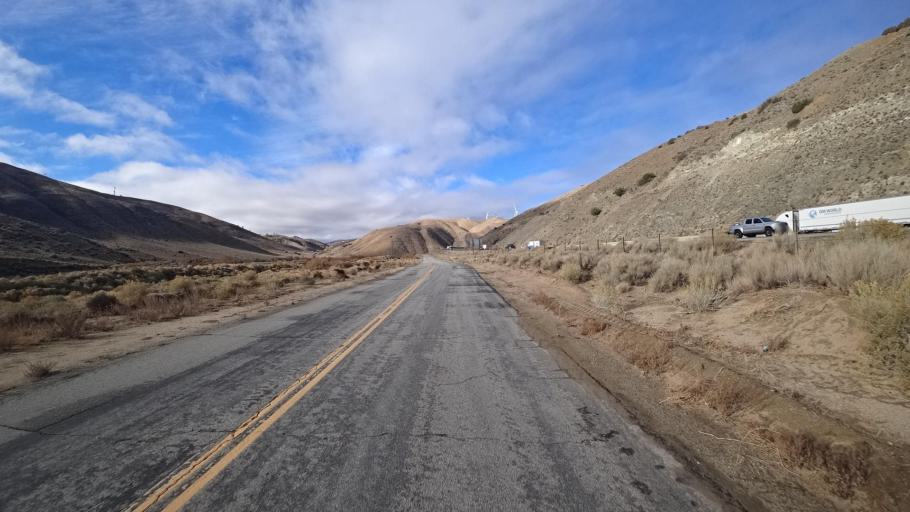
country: US
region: California
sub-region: Kern County
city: Mojave
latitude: 35.0982
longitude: -118.2962
